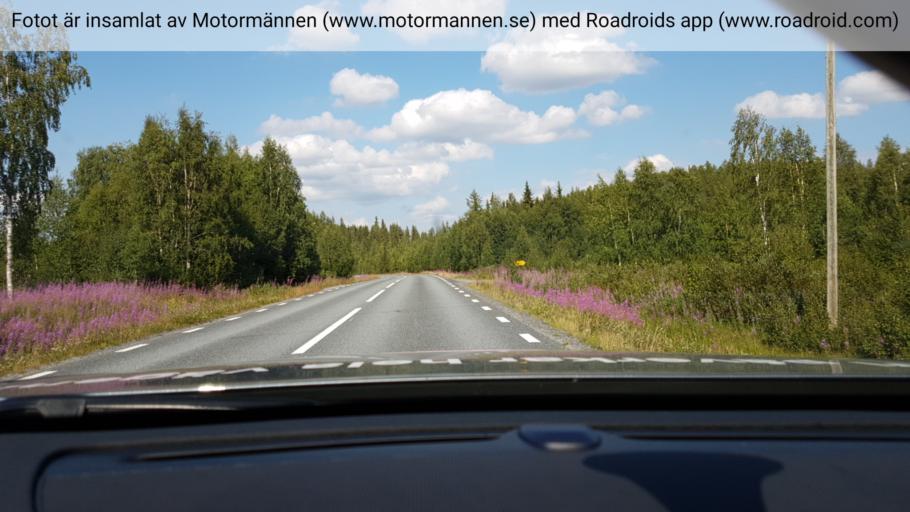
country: SE
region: Vaesterbotten
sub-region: Sorsele Kommun
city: Sorsele
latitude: 65.3704
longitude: 17.5752
